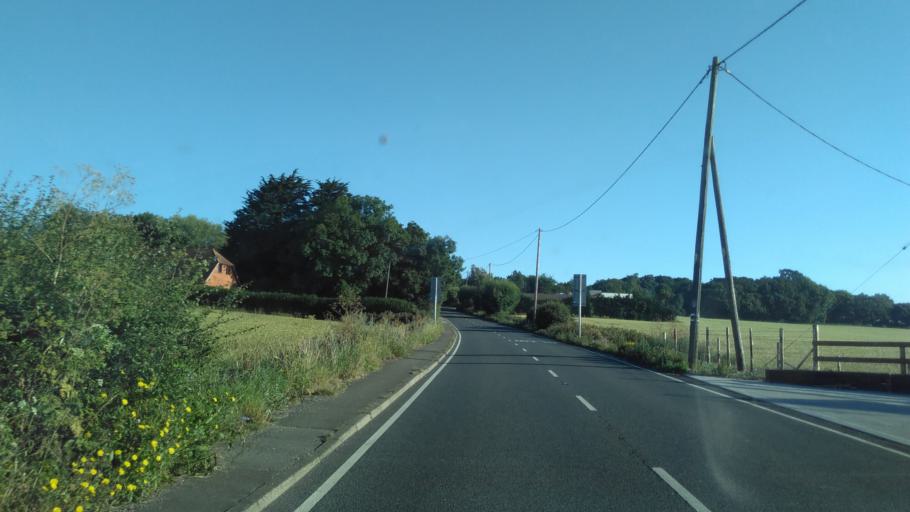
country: GB
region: England
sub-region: Kent
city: Whitstable
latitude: 51.3334
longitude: 1.0237
